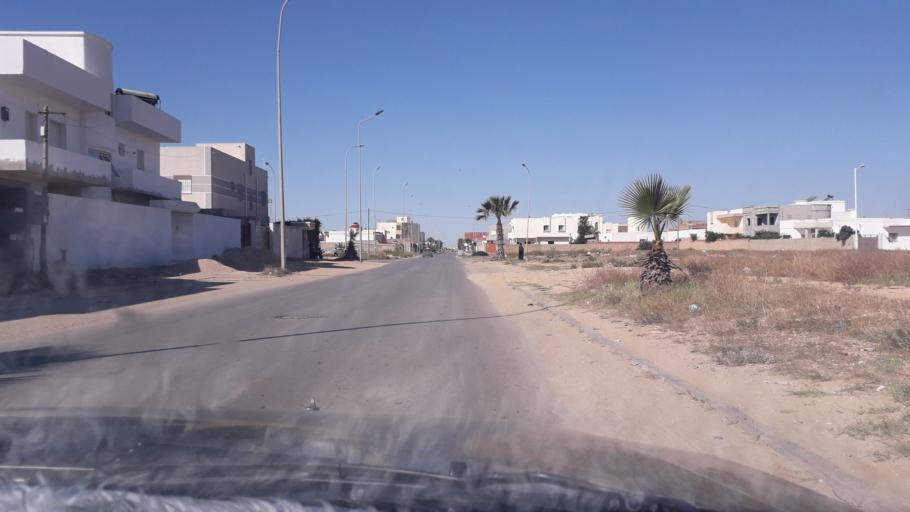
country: TN
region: Safaqis
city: Al Qarmadah
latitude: 34.8277
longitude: 10.7526
